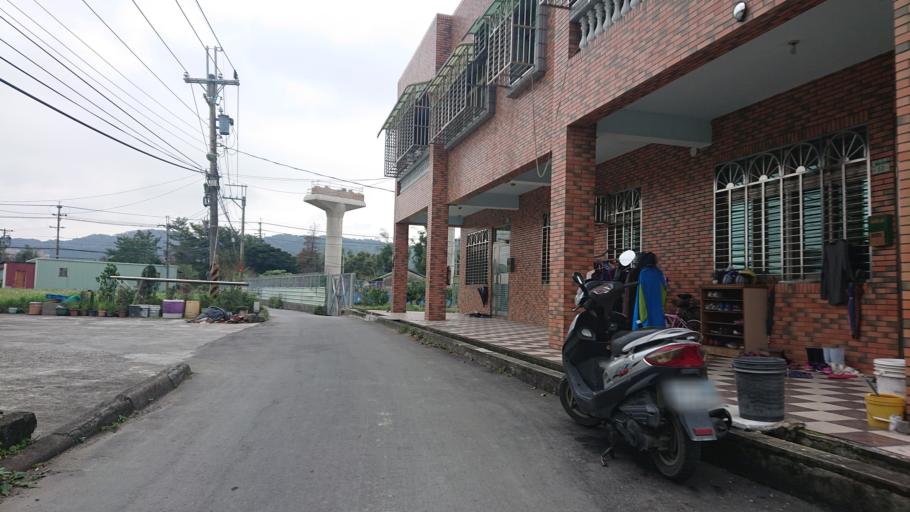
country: TW
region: Taiwan
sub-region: Taoyuan
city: Taoyuan
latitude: 24.9466
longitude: 121.3656
